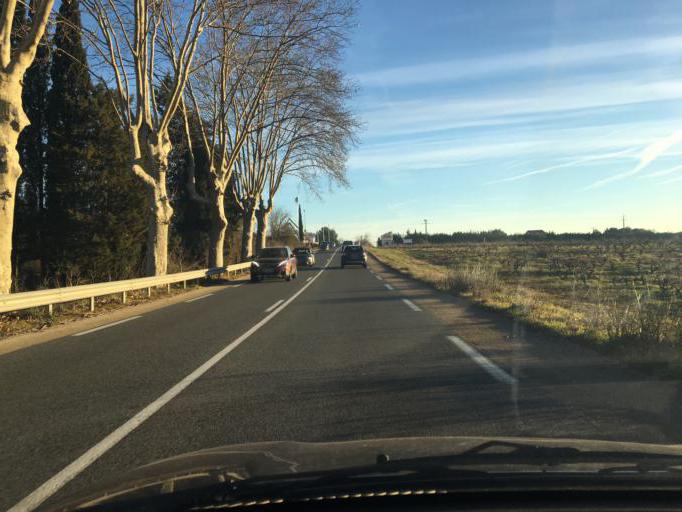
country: FR
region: Provence-Alpes-Cote d'Azur
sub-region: Departement du Var
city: La Motte
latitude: 43.4629
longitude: 6.5315
